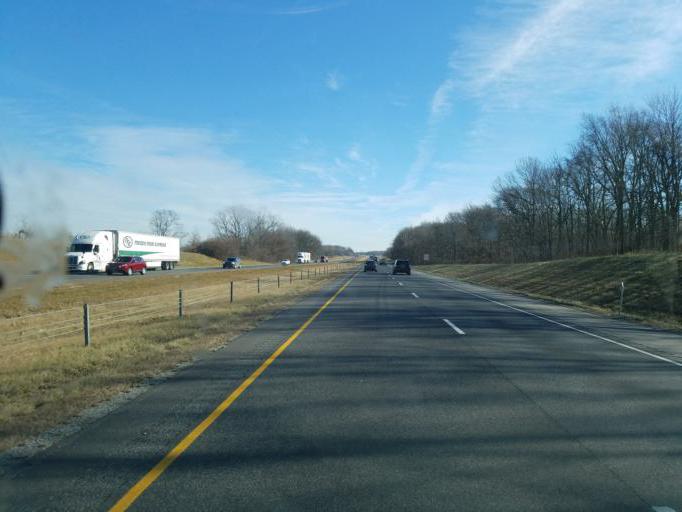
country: US
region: Indiana
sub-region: Henry County
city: Knightstown
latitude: 39.8446
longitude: -85.5385
